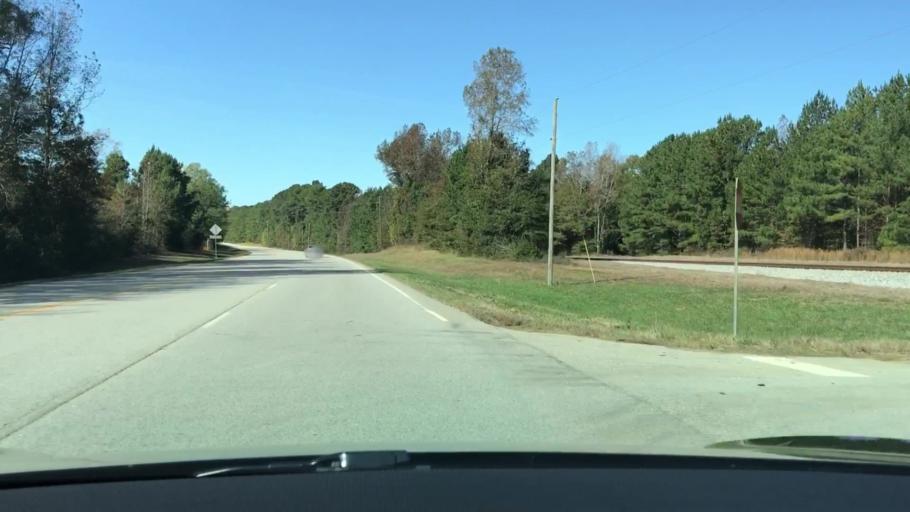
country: US
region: Georgia
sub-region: Warren County
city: Firing Range
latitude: 33.4782
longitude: -82.7352
